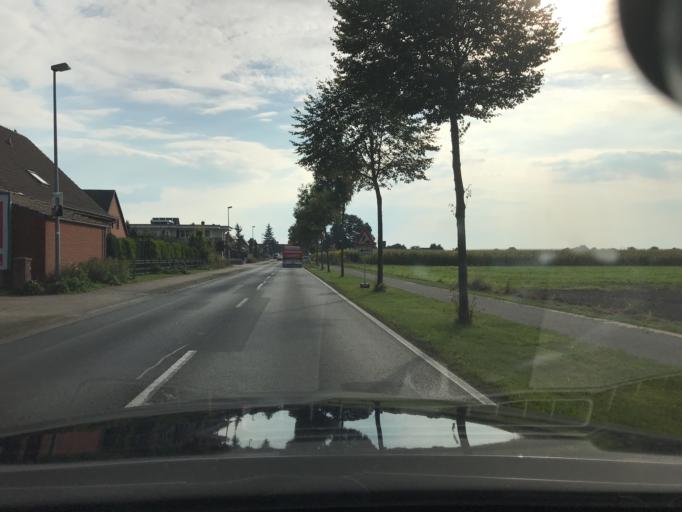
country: DE
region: Lower Saxony
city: Riede
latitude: 52.9777
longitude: 8.8748
